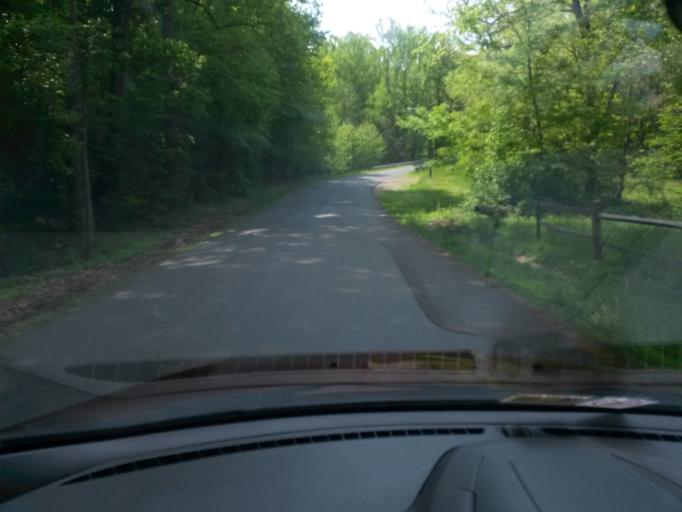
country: US
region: Virginia
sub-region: Campbell County
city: Timberlake
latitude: 37.3507
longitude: -79.2180
